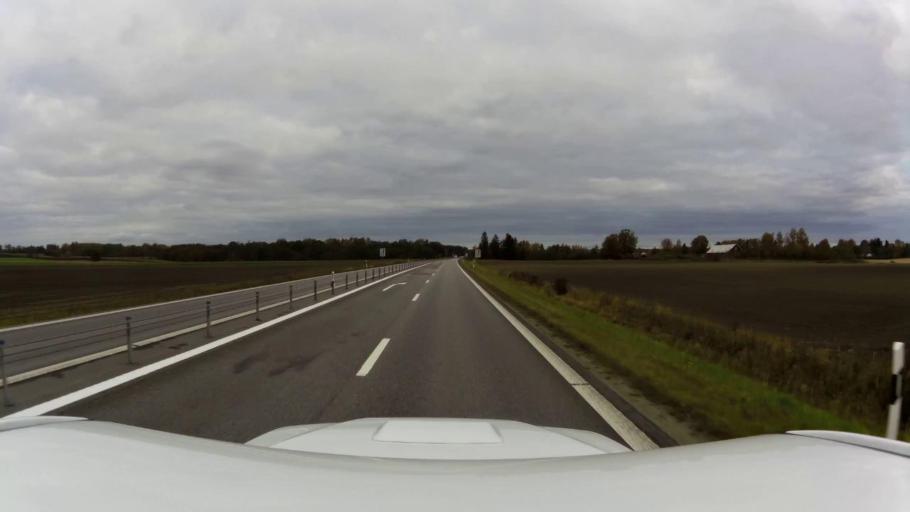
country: SE
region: OEstergoetland
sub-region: Linkopings Kommun
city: Malmslatt
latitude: 58.4501
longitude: 15.5074
